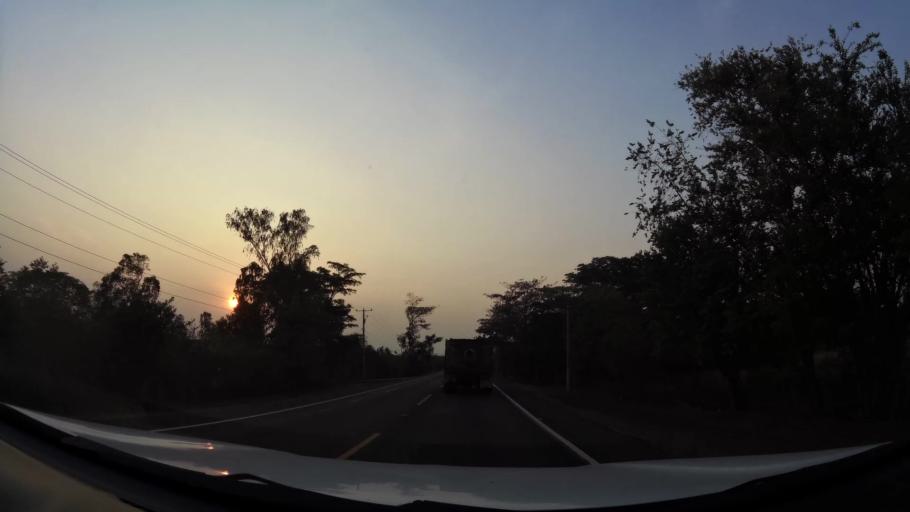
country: NI
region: Leon
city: La Paz Centro
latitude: 12.3100
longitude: -86.7830
